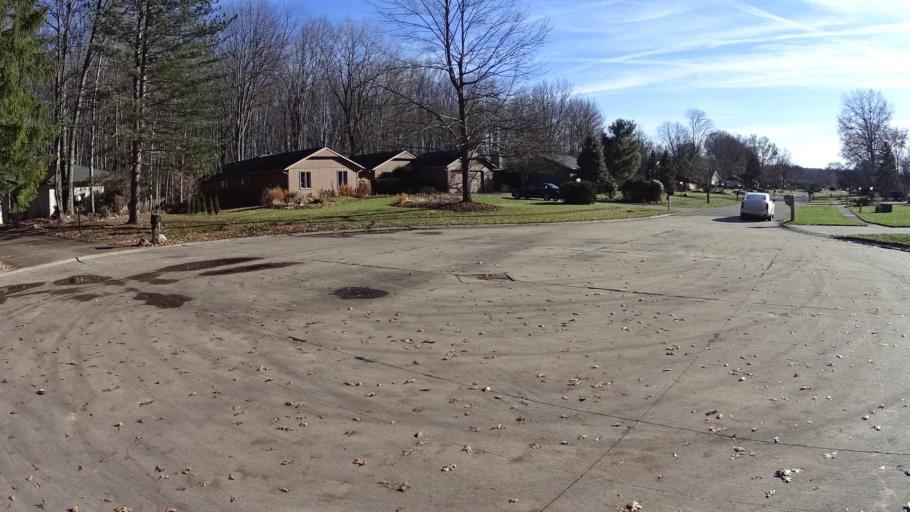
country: US
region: Ohio
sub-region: Cuyahoga County
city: North Olmsted
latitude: 41.4037
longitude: -81.9711
